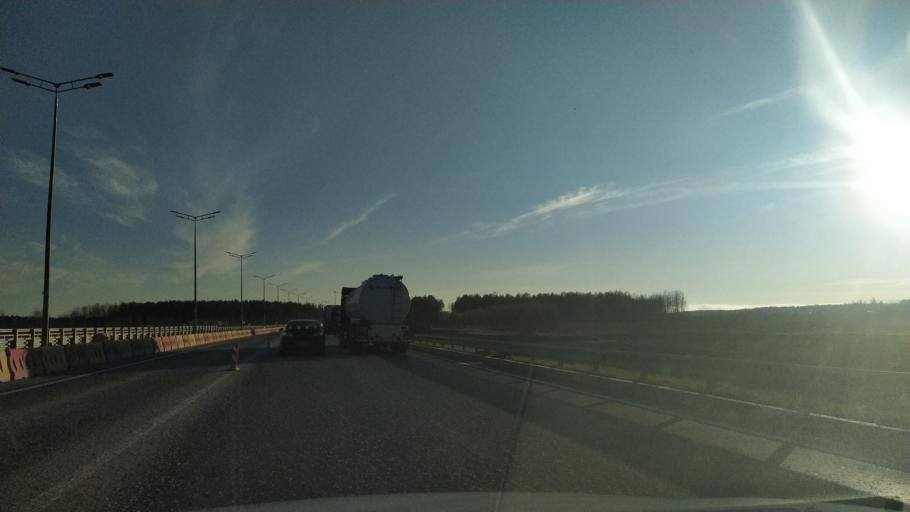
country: RU
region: St.-Petersburg
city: Levashovo
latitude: 60.0872
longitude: 30.2323
